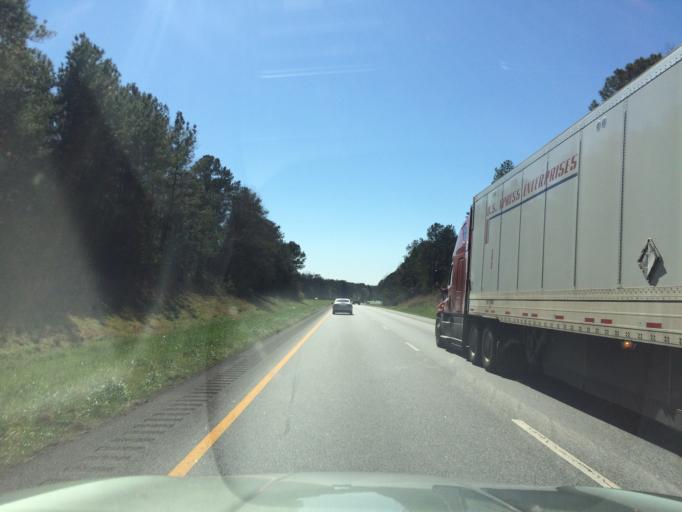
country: US
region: Alabama
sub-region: Macon County
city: Tuskegee
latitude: 32.4955
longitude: -85.6211
